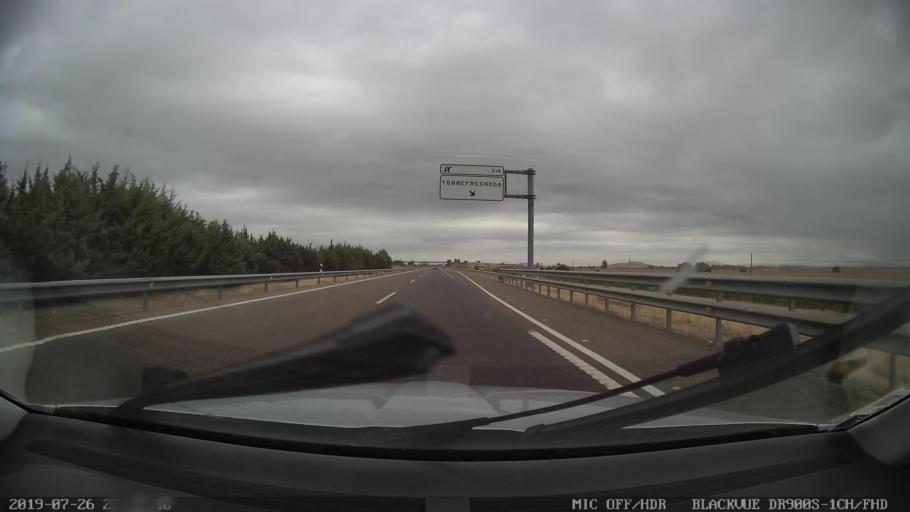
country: ES
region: Extremadura
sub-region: Provincia de Badajoz
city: San Pedro de Merida
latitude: 38.9889
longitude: -6.1281
